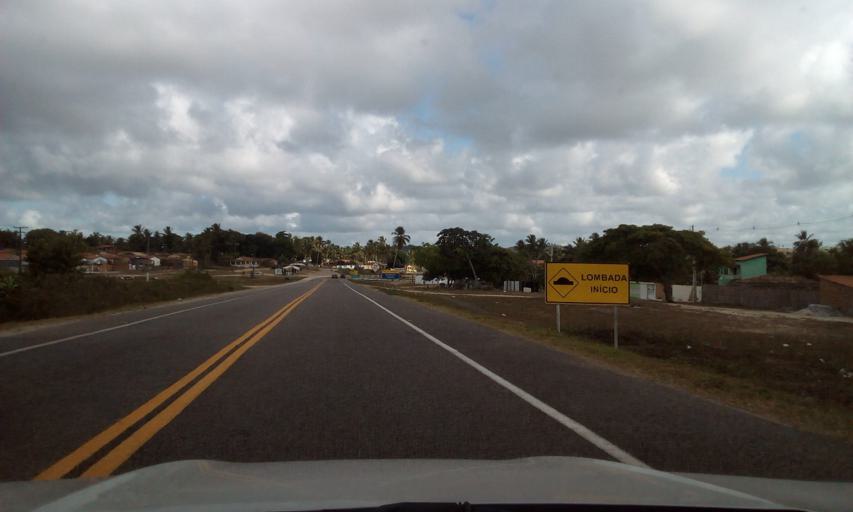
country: BR
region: Bahia
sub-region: Conde
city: Conde
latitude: -11.7965
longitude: -37.6271
